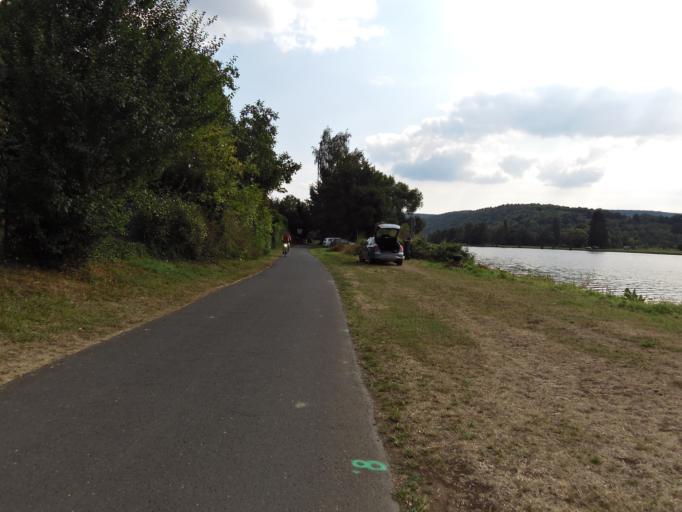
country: DE
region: Bavaria
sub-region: Regierungsbezirk Unterfranken
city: Klingenberg am Main
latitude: 49.7744
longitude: 9.1833
